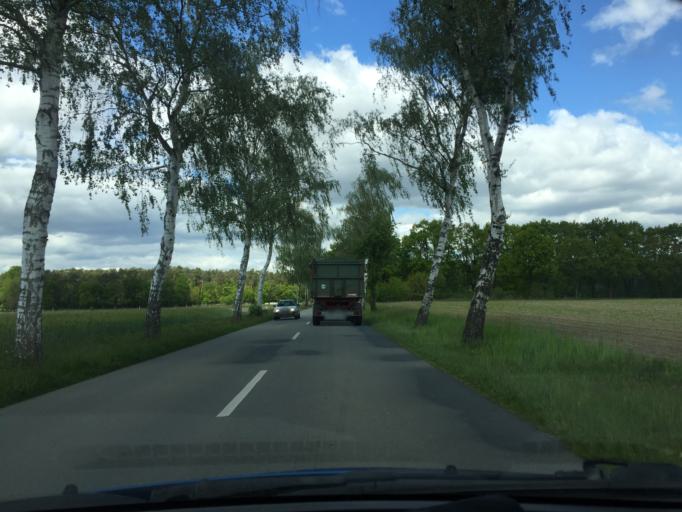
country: DE
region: Lower Saxony
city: Suderburg
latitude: 52.9216
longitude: 10.5010
